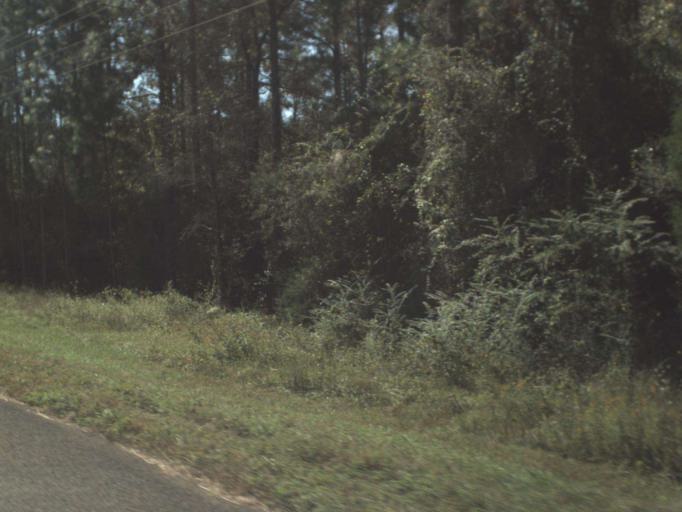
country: US
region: Florida
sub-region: Walton County
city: DeFuniak Springs
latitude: 30.8843
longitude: -86.1257
